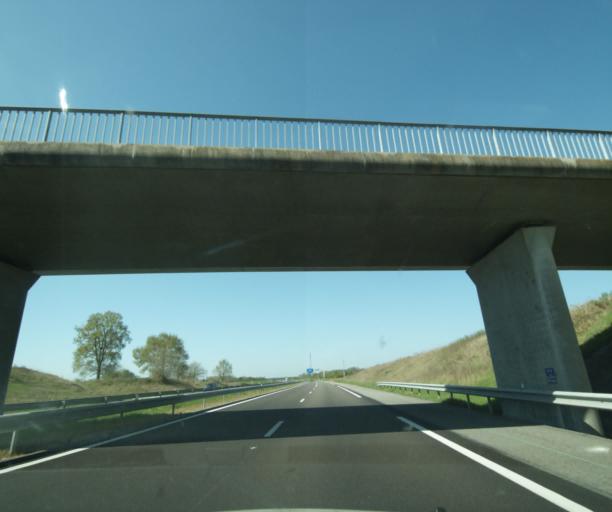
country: FR
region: Centre
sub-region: Departement du Loiret
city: Bonny-sur-Loire
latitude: 47.5653
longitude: 2.8800
